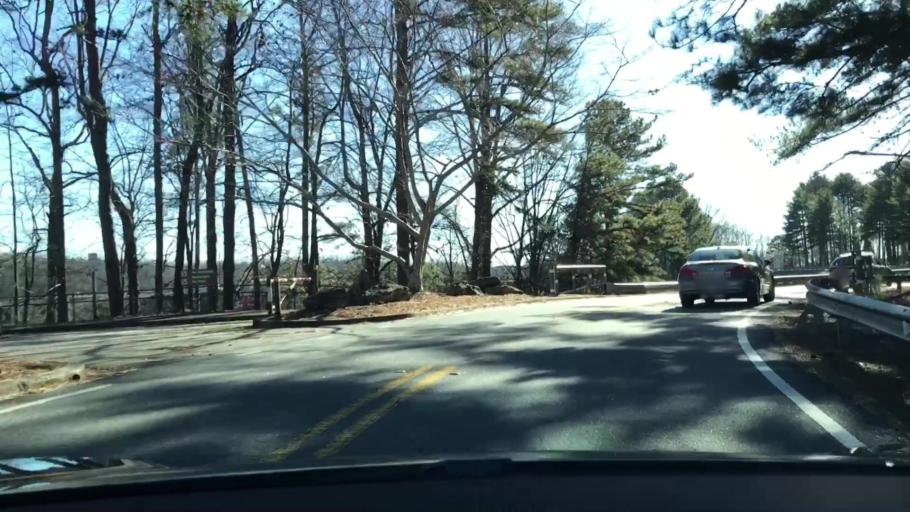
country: US
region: Georgia
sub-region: Gwinnett County
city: Sugar Hill
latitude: 34.1649
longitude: -84.0758
